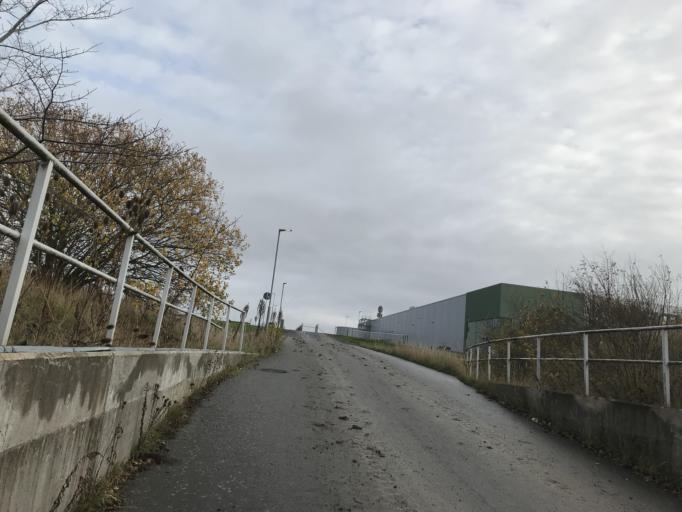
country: SE
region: Skane
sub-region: Landskrona
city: Landskrona
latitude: 55.8767
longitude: 12.8602
